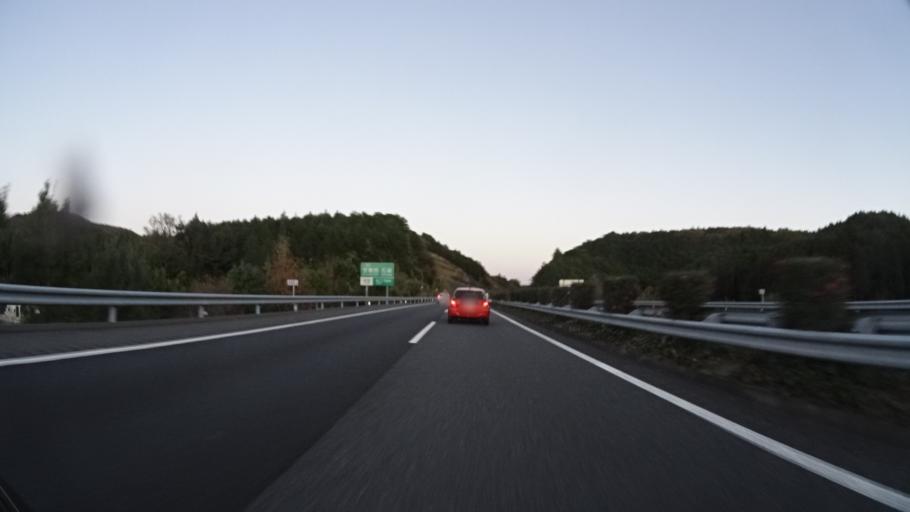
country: JP
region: Ibaraki
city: Iwase
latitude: 36.3482
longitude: 140.1603
